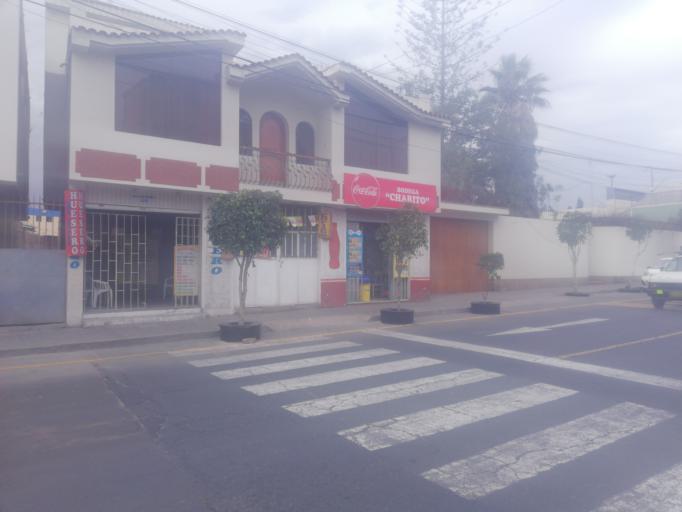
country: PE
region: Arequipa
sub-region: Provincia de Arequipa
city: Tiabaya
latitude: -16.4494
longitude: -71.5892
